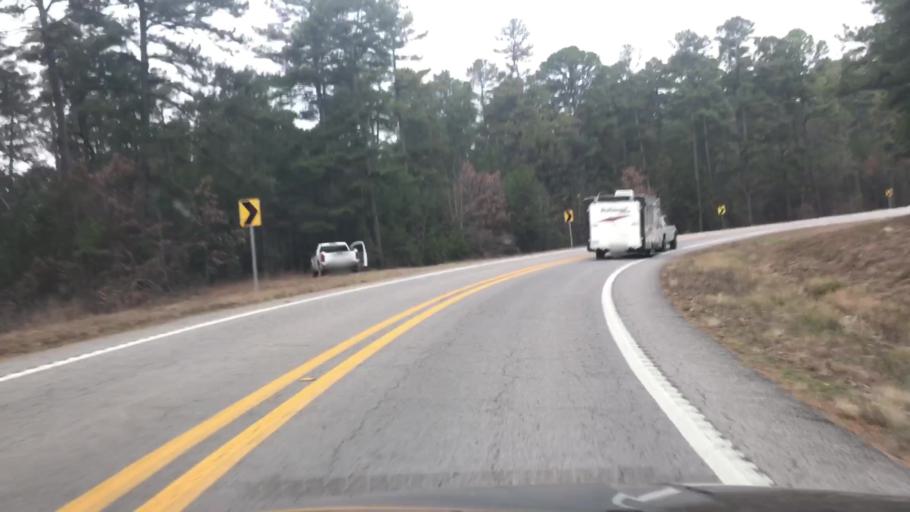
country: US
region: Arkansas
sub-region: Montgomery County
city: Mount Ida
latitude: 34.6729
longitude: -93.7853
